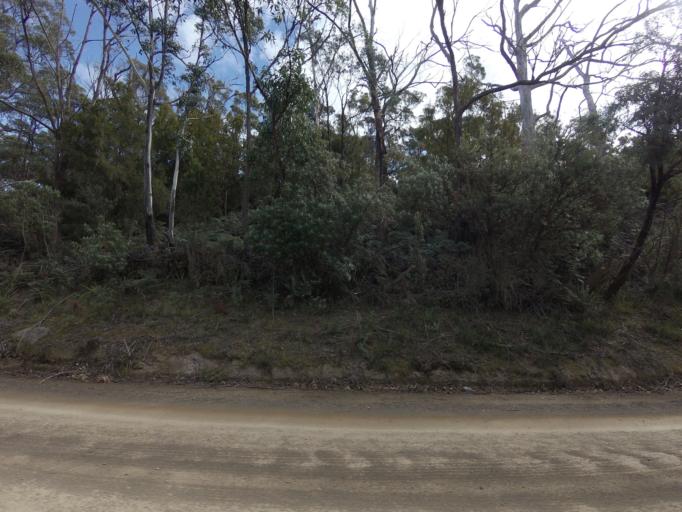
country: AU
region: Tasmania
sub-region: Clarence
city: Sandford
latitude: -43.0928
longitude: 147.7306
